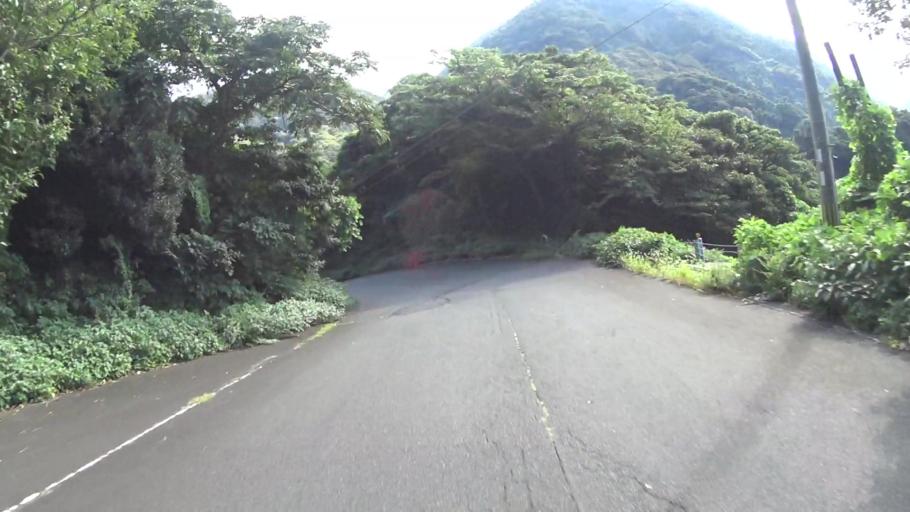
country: JP
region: Kyoto
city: Miyazu
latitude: 35.7726
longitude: 135.2248
